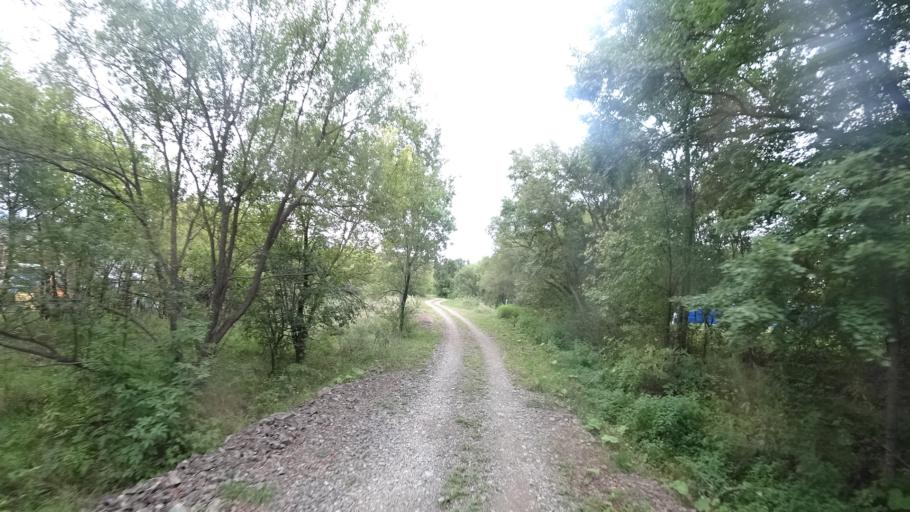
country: RU
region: Primorskiy
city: Monastyrishche
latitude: 44.2684
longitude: 132.4561
